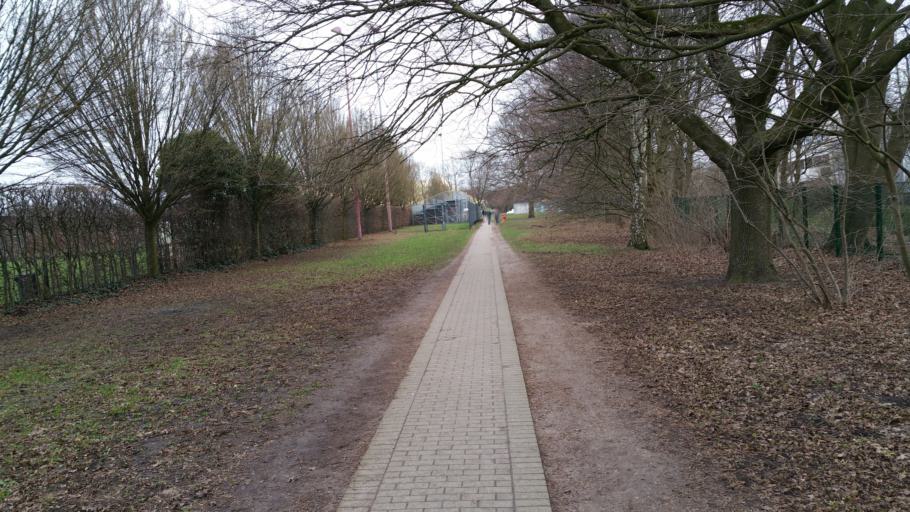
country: DE
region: Hamburg
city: Stellingen
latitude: 53.5885
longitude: 9.9461
